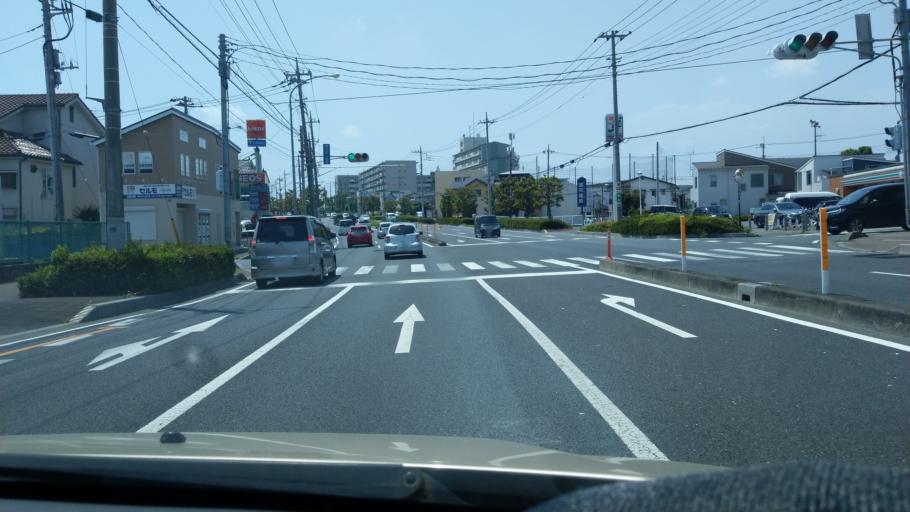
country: JP
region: Saitama
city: Saitama
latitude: 35.8731
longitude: 139.6736
